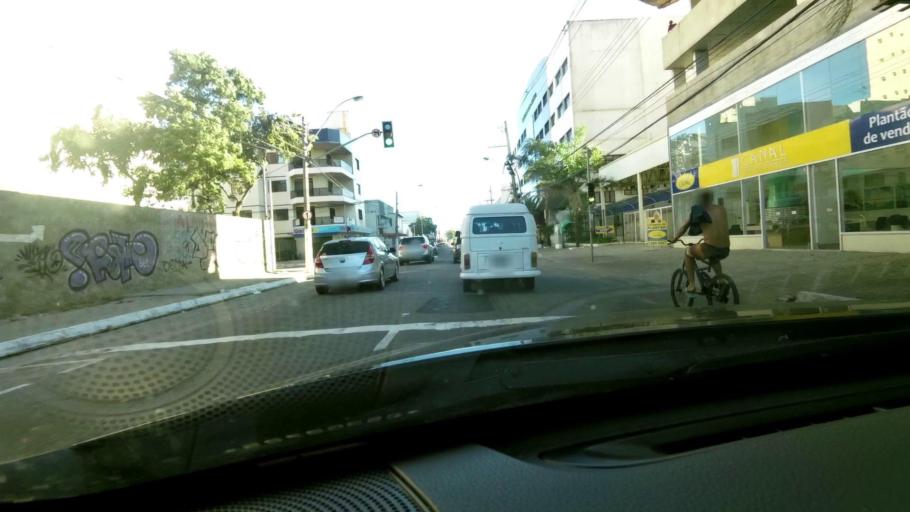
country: BR
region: Espirito Santo
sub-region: Vila Velha
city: Vila Velha
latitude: -20.3589
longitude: -40.2979
